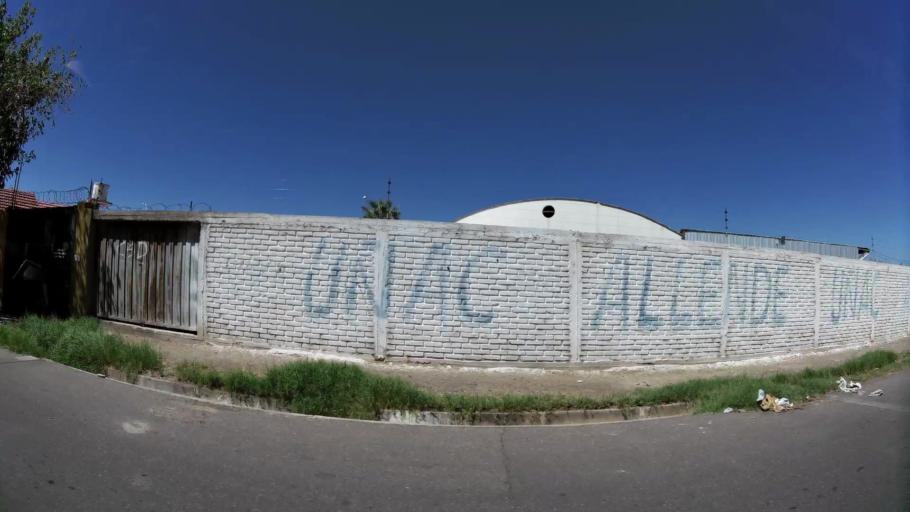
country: AR
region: San Juan
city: San Juan
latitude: -31.5215
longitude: -68.5375
